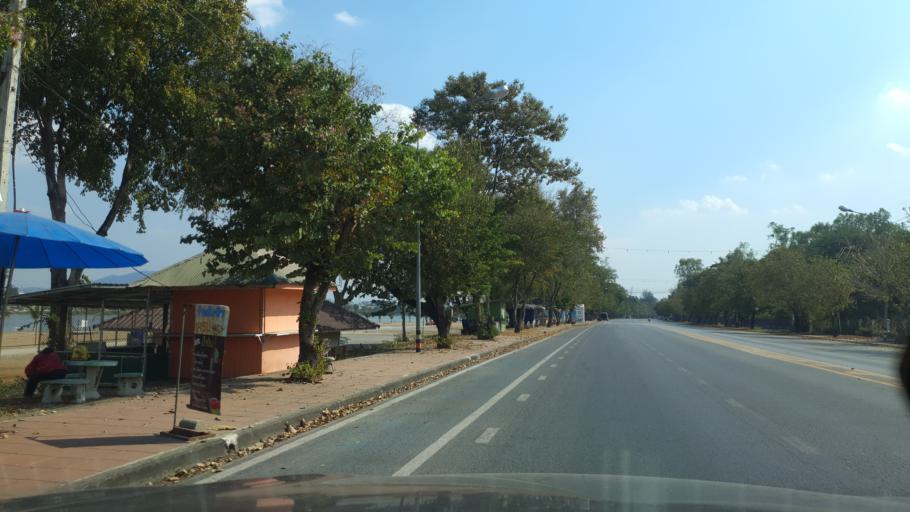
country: TH
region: Tak
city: Tak
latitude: 16.8809
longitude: 99.1144
